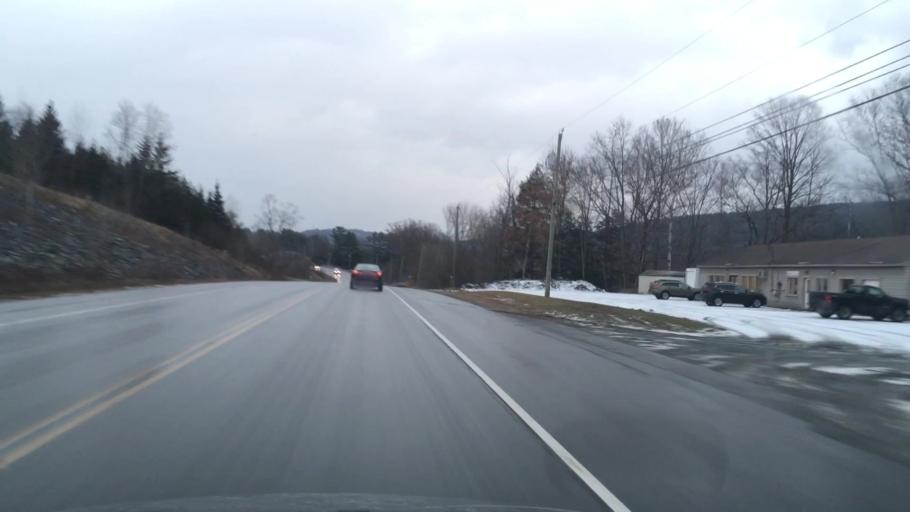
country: US
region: New Hampshire
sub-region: Sullivan County
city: Claremont
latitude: 43.3646
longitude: -72.2942
